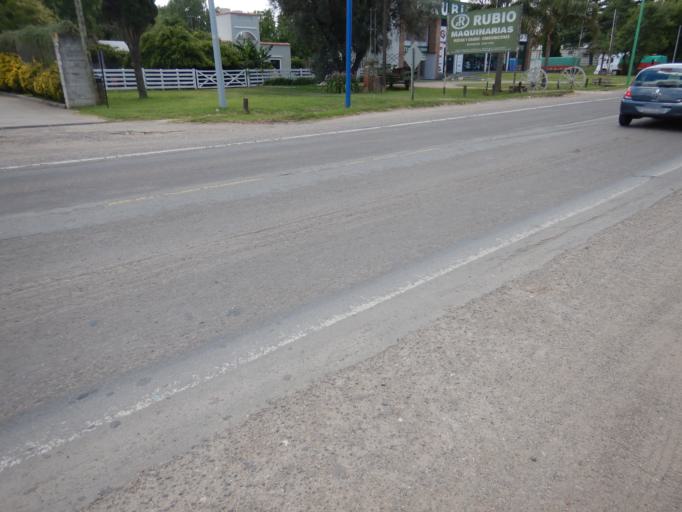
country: AR
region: Santa Fe
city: Canada de Gomez
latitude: -32.8079
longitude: -61.4092
